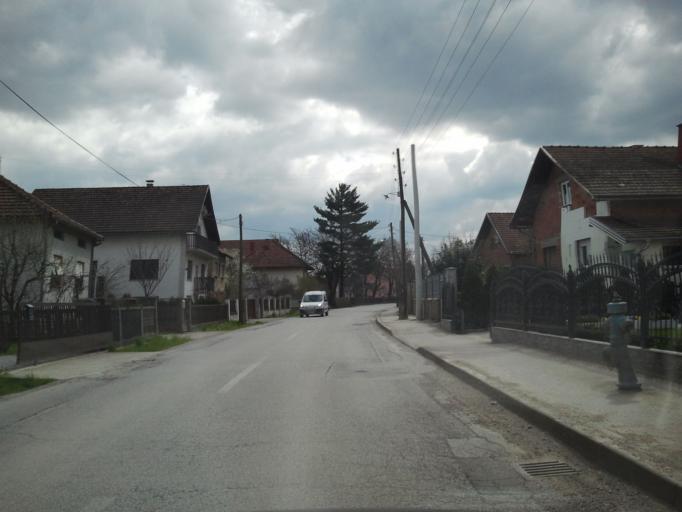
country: HR
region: Grad Zagreb
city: Brezovica
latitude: 45.7318
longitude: 15.8999
